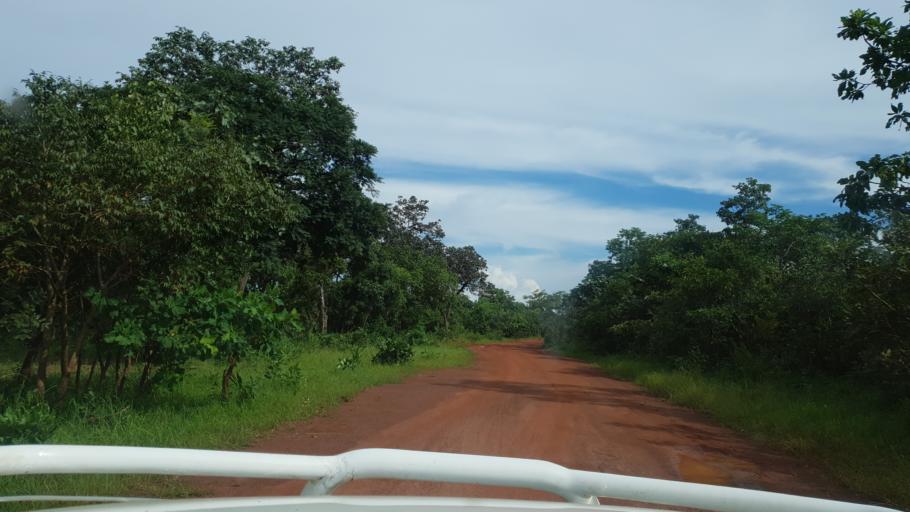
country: ML
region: Sikasso
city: Kolondieba
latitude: 10.7431
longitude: -6.9113
